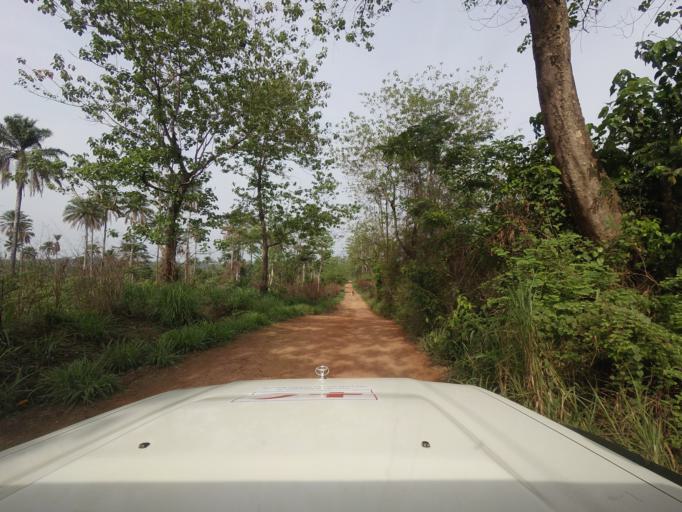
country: GN
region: Nzerekore
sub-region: Macenta
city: Macenta
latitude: 8.5396
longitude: -9.4948
